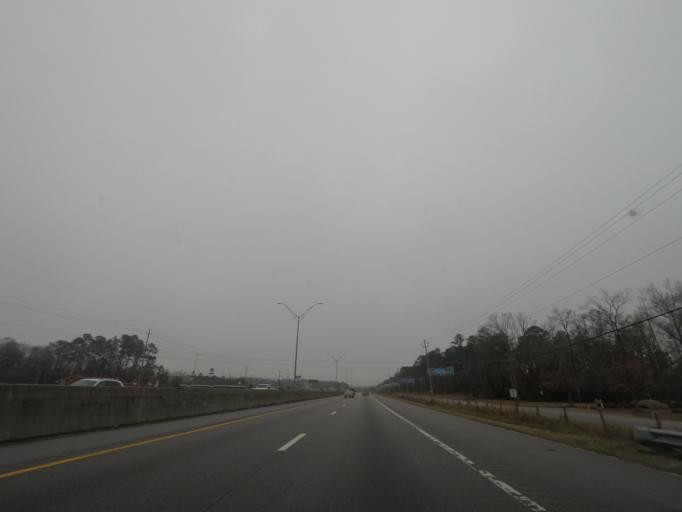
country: US
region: North Carolina
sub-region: Robeson County
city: Lumberton
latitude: 34.6614
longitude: -79.0089
